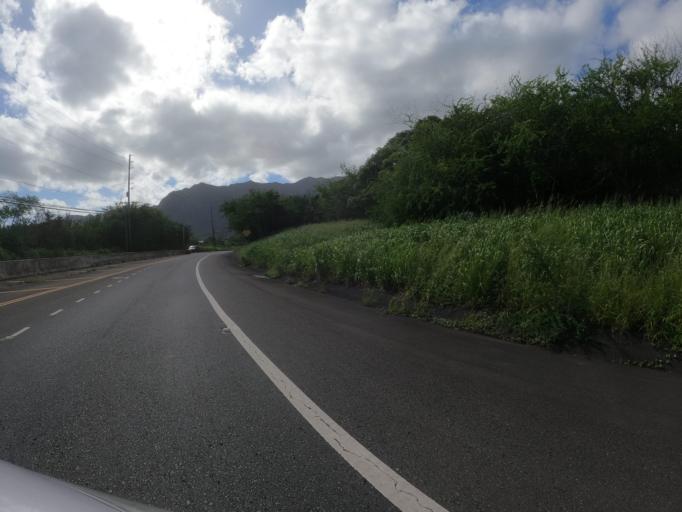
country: US
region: Hawaii
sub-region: Honolulu County
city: Waimanalo
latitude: 21.3545
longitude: -157.7307
